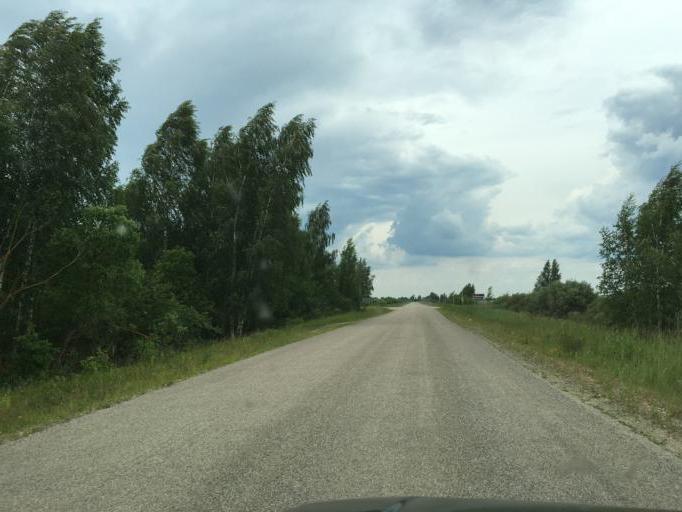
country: LV
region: Vilanu
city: Vilani
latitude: 56.7644
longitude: 26.9716
